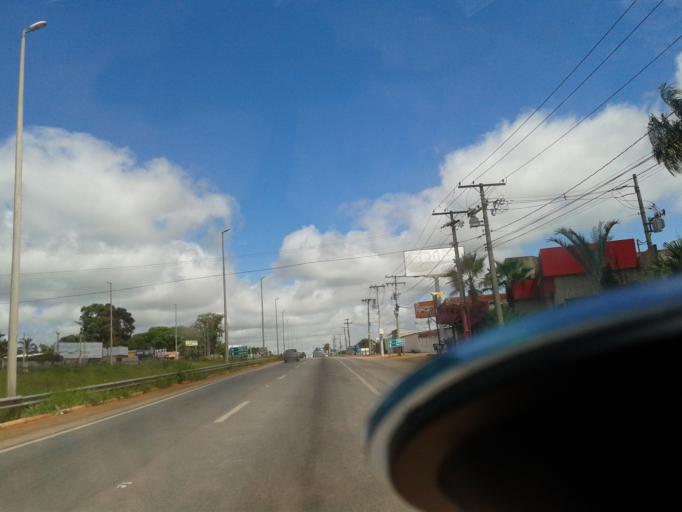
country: BR
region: Goias
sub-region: Goiania
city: Goiania
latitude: -16.6285
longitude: -49.3507
